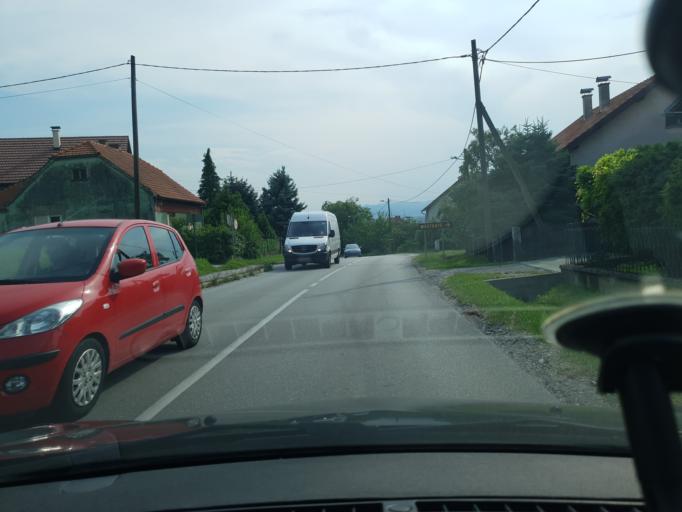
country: HR
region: Zagrebacka
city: Jablanovec
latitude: 45.8775
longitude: 15.8508
